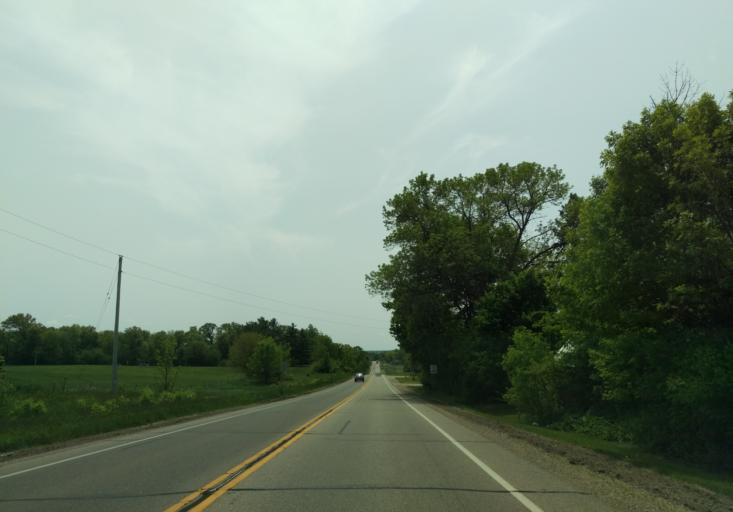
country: US
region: Wisconsin
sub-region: Rock County
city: Evansville
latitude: 42.7973
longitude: -89.2992
